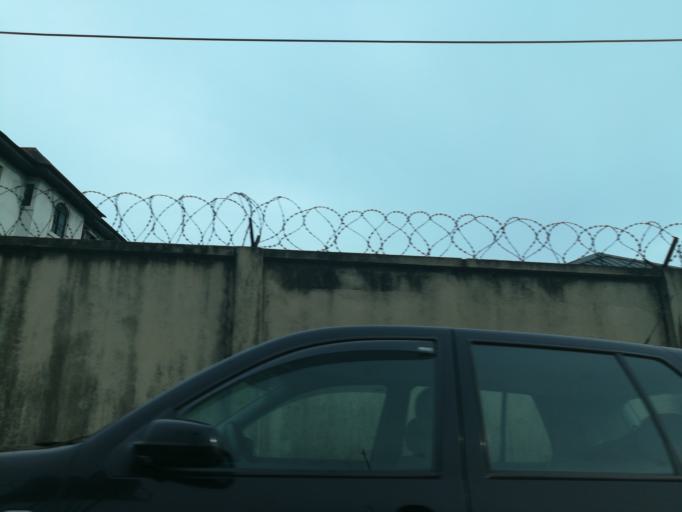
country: NG
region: Rivers
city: Port Harcourt
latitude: 4.8098
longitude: 6.9998
